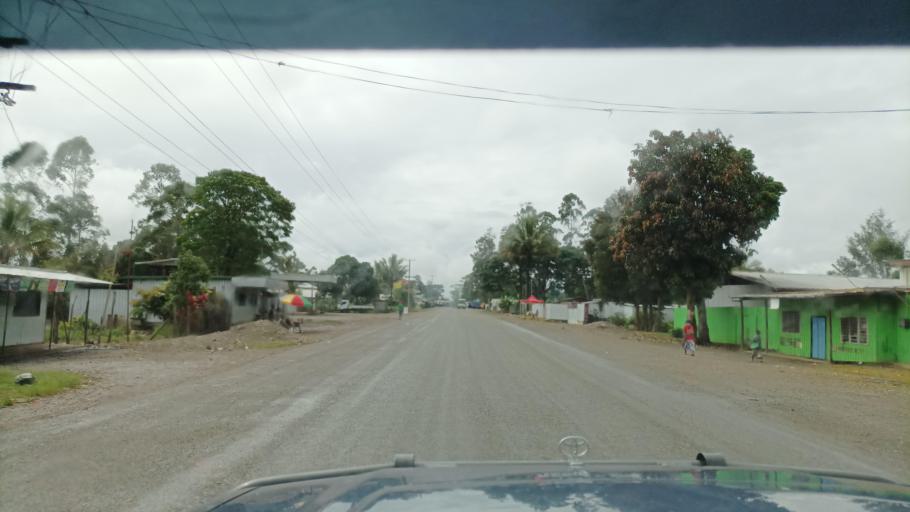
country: PG
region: Jiwaka
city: Minj
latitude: -5.8799
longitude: 144.6773
